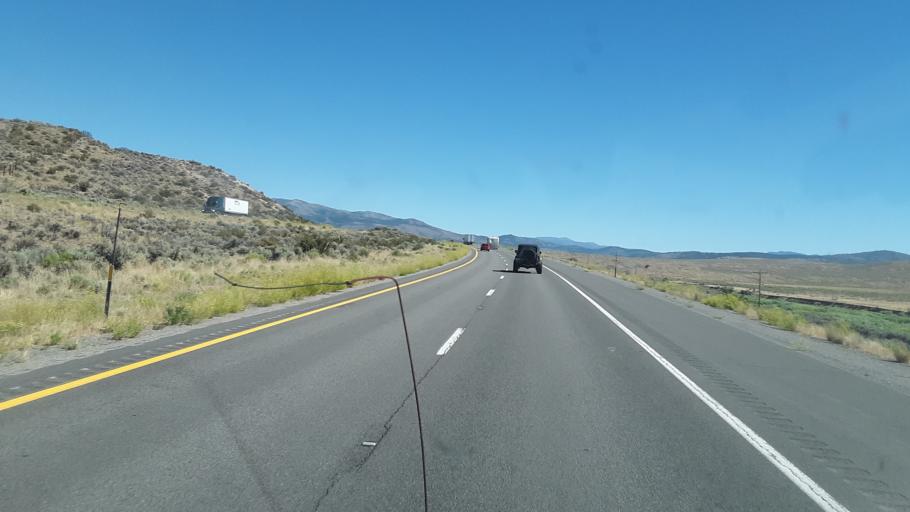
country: US
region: Nevada
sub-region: Washoe County
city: Cold Springs
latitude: 39.7048
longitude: -120.0340
